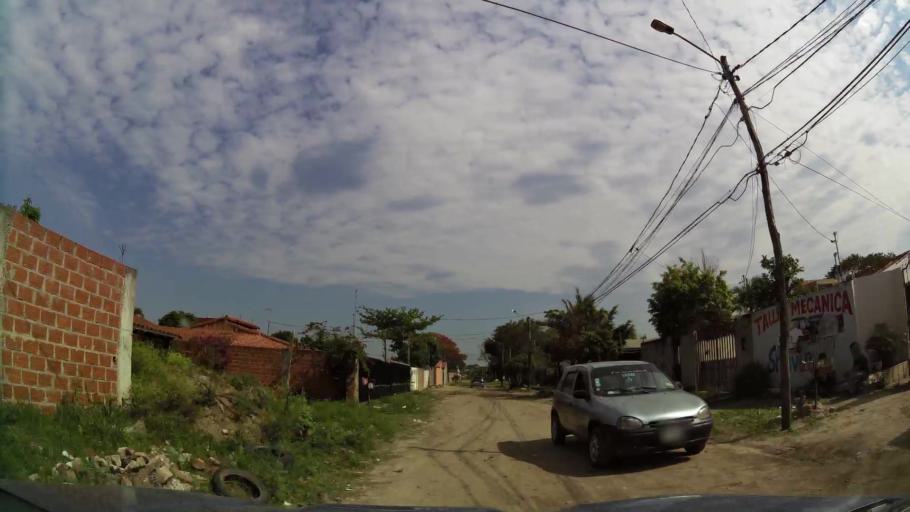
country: BO
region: Santa Cruz
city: Santa Cruz de la Sierra
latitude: -17.7282
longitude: -63.1749
